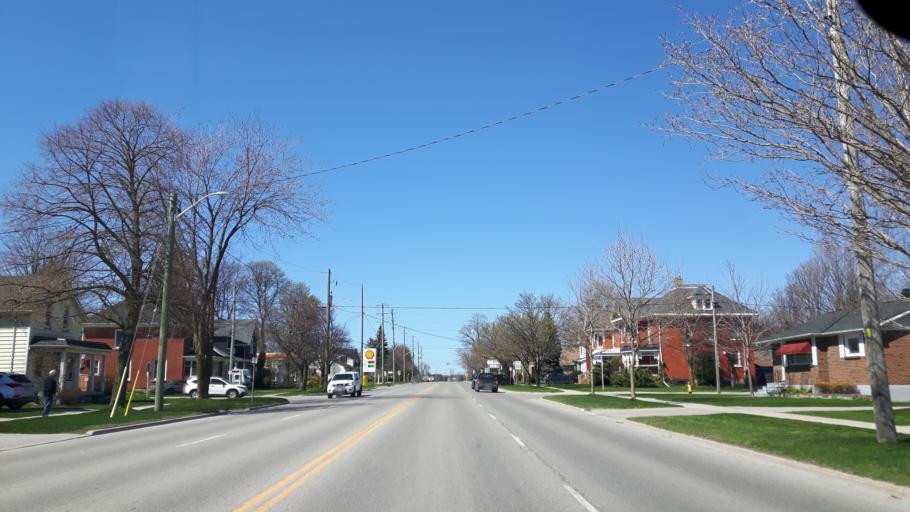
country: CA
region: Ontario
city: Goderich
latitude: 43.7466
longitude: -81.7078
